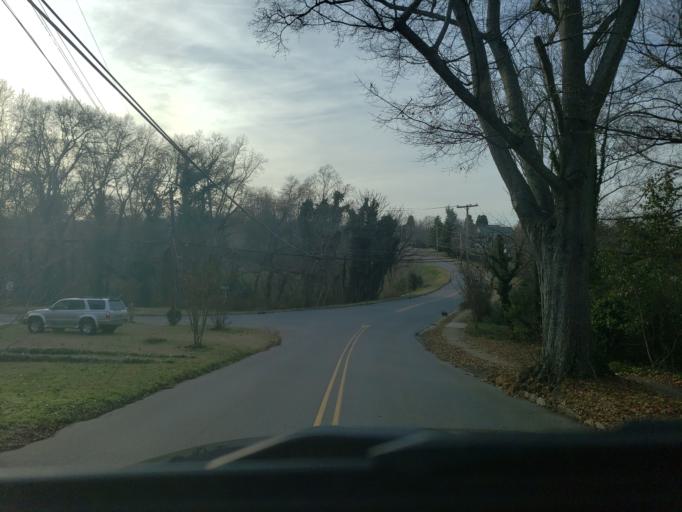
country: US
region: North Carolina
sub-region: Cleveland County
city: Shelby
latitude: 35.2891
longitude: -81.5310
